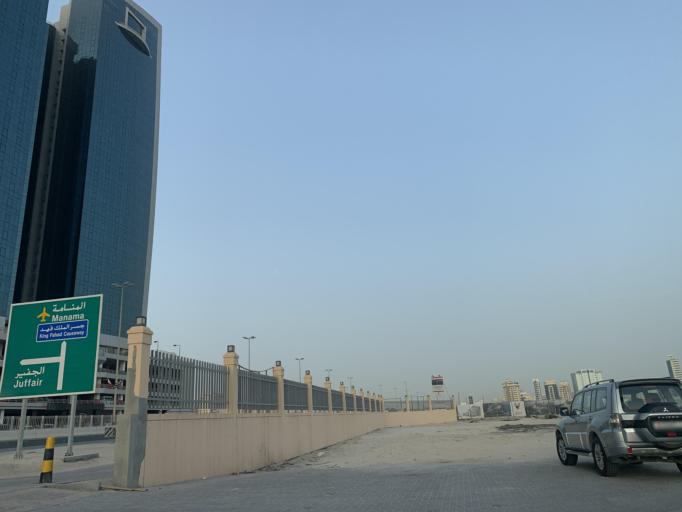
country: BH
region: Manama
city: Manama
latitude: 26.2243
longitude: 50.6080
